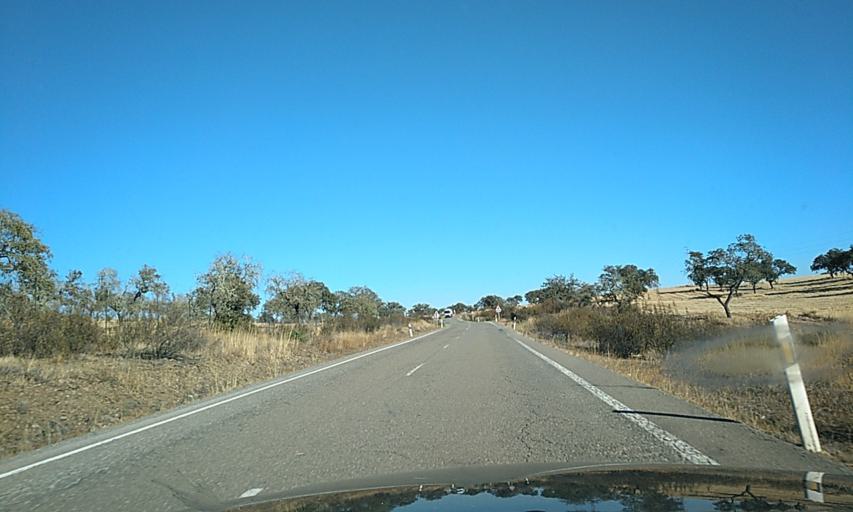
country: ES
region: Andalusia
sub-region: Provincia de Huelva
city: Santa Barbara de Casa
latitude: 37.7758
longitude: -7.1502
